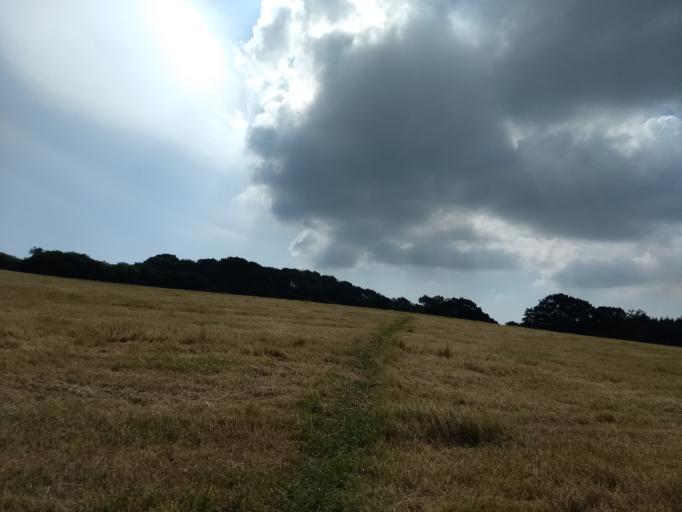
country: GB
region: England
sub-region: Isle of Wight
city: Ryde
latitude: 50.7107
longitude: -1.1536
